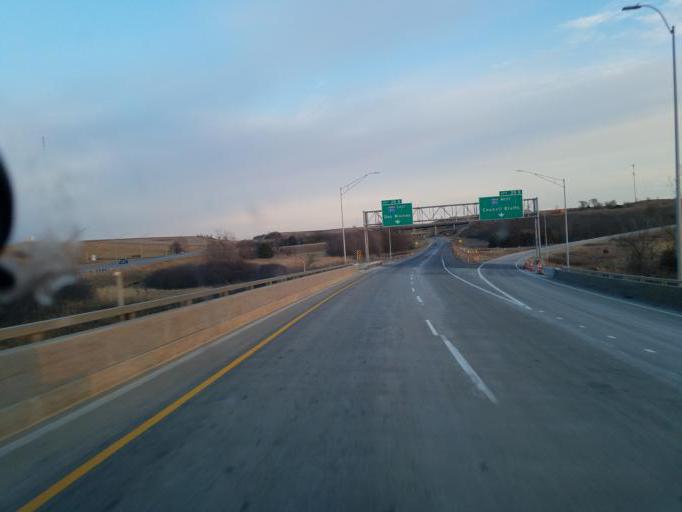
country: US
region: Iowa
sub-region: Harrison County
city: Logan
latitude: 41.4986
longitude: -95.5910
